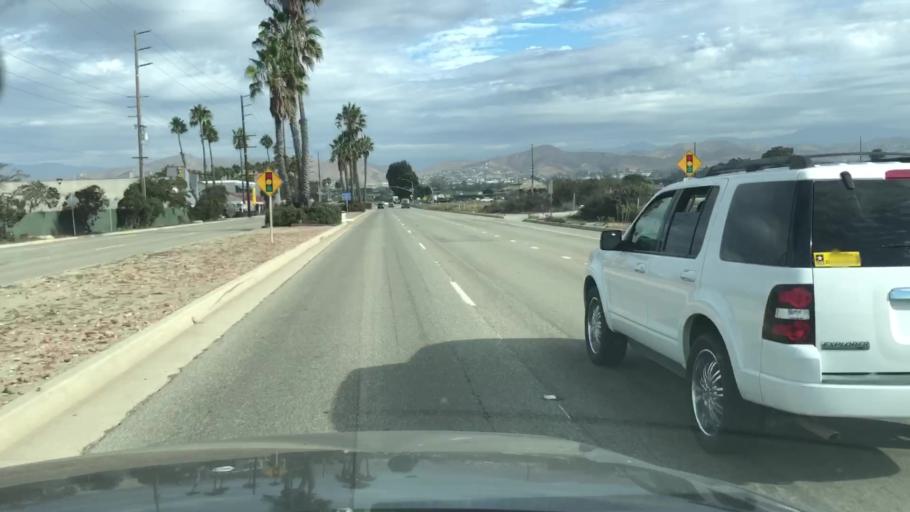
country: US
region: California
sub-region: Ventura County
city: Ventura
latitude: 34.2413
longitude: -119.2567
